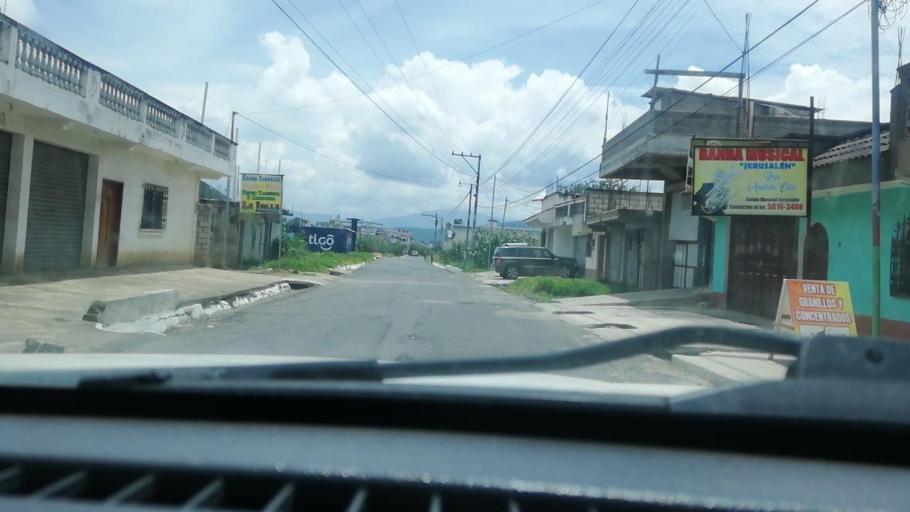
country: GT
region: Totonicapan
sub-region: Municipio de San Andres Xecul
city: San Andres Xecul
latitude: 14.9050
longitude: -91.4755
